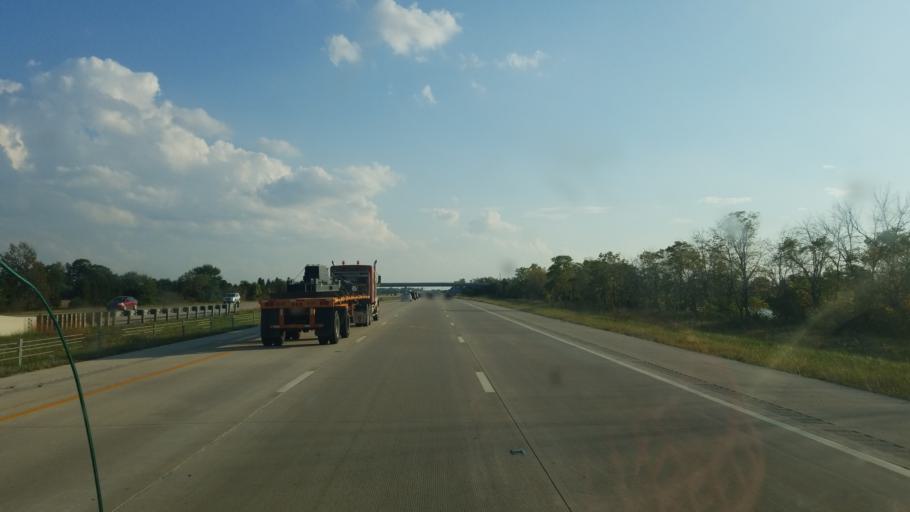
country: US
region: Ohio
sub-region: Wood County
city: Perrysburg
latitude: 41.5107
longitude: -83.6222
